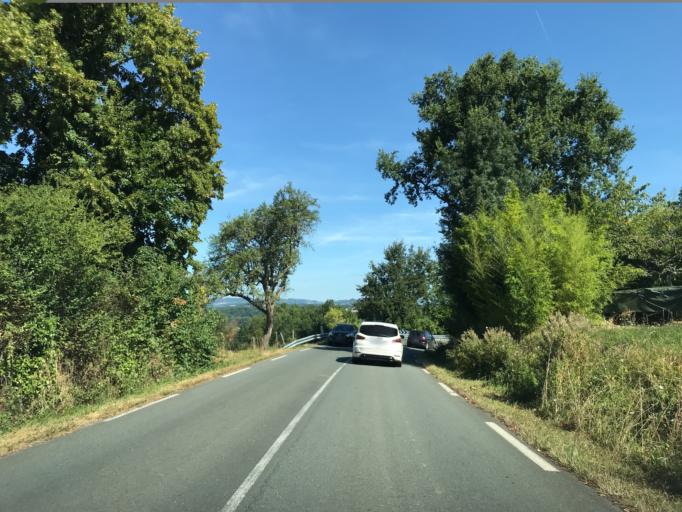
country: FR
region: Limousin
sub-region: Departement de la Correze
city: Larche
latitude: 45.1137
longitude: 1.3969
